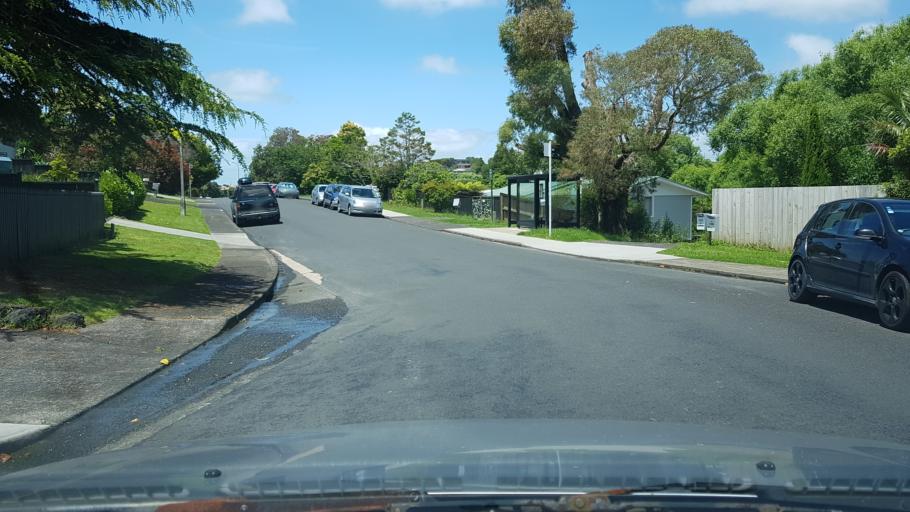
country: NZ
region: Auckland
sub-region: Auckland
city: North Shore
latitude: -36.7970
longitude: 174.7284
